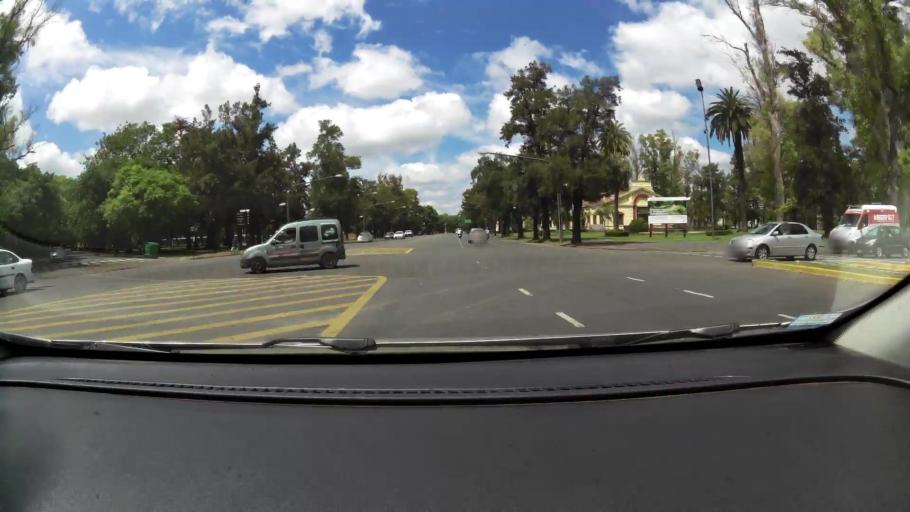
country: AR
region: Santa Fe
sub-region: Departamento de Rosario
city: Rosario
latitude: -32.9624
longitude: -60.6581
